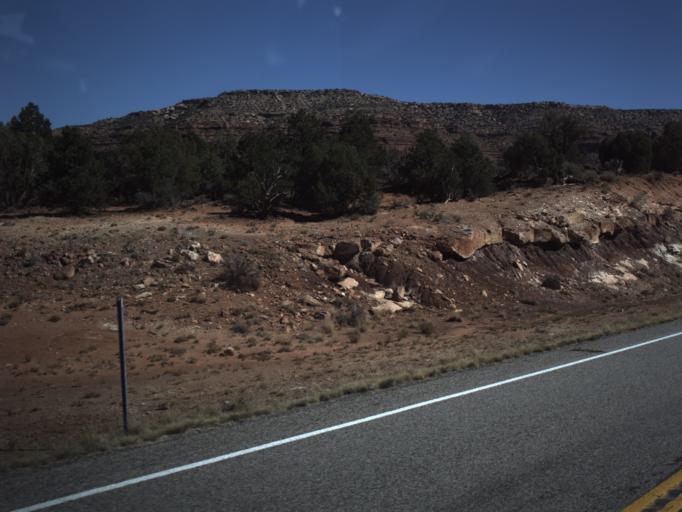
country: US
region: Utah
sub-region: San Juan County
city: Blanding
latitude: 37.6357
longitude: -110.1554
